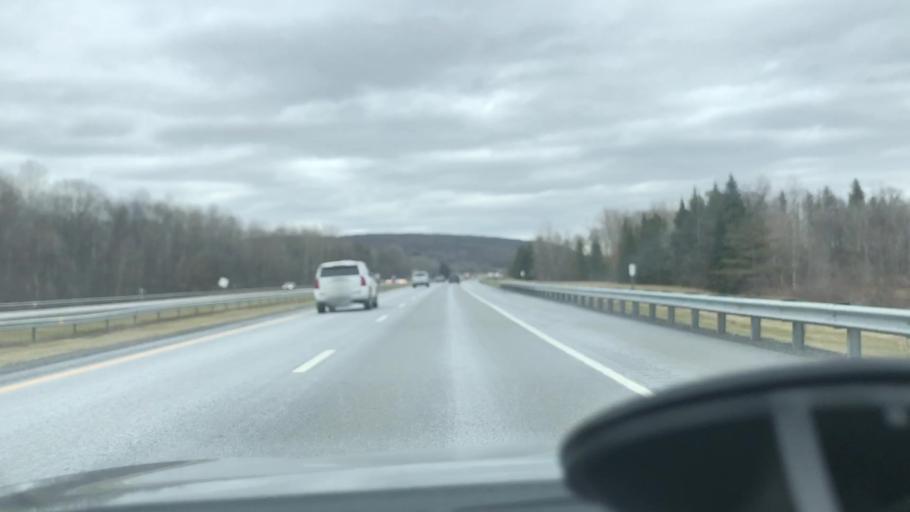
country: US
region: New York
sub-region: Herkimer County
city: Frankfort
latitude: 43.0595
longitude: -75.0741
